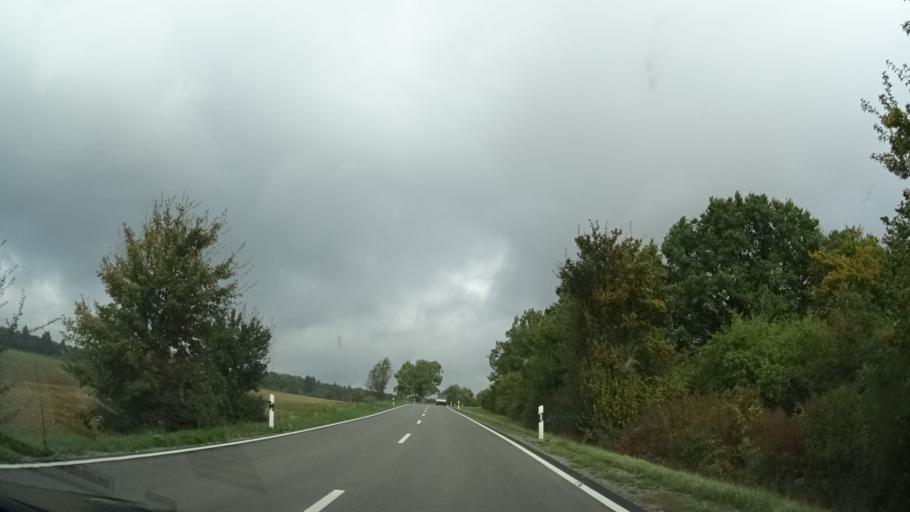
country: DE
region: Baden-Wuerttemberg
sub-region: Karlsruhe Region
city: Konigsbach-Stein
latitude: 48.9797
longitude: 8.6388
